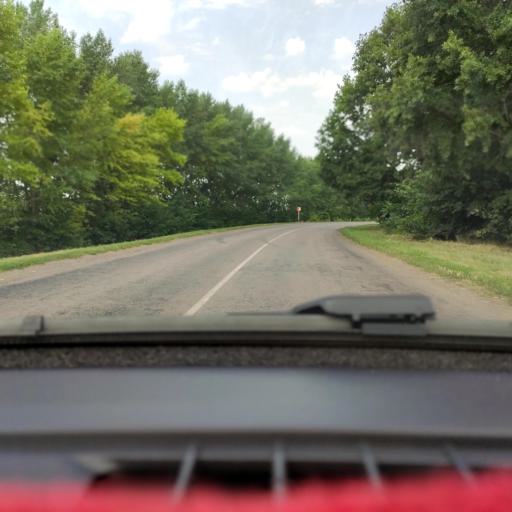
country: RU
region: Voronezj
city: Kashirskoye
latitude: 51.2443
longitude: 39.6134
